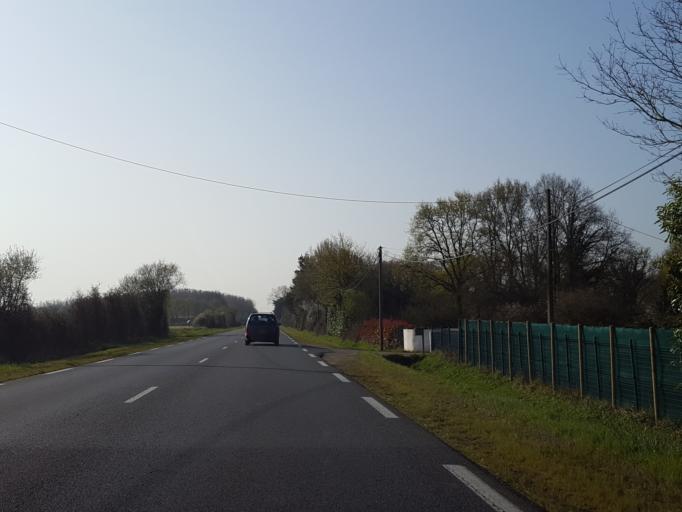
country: FR
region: Pays de la Loire
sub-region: Departement de la Loire-Atlantique
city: Geneston
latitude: 47.0775
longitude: -1.5233
